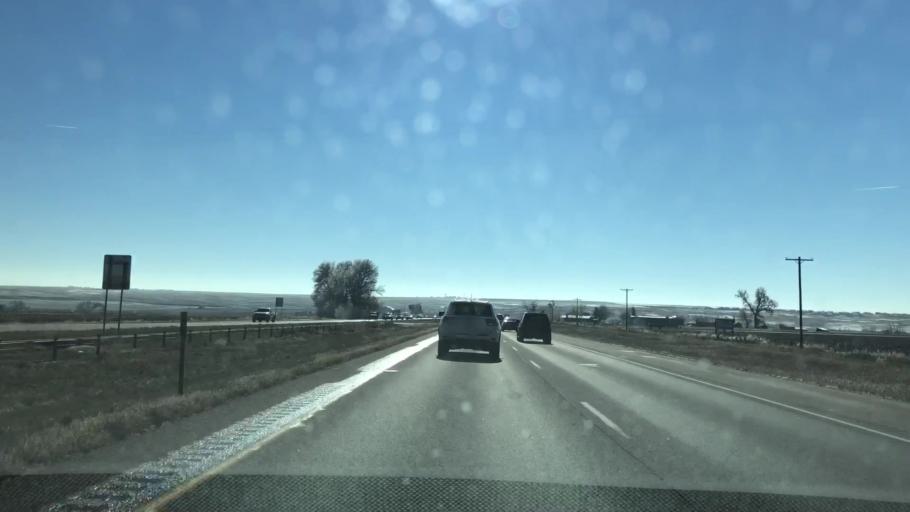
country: US
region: Colorado
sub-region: Weld County
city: Johnstown
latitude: 40.3164
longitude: -104.9803
